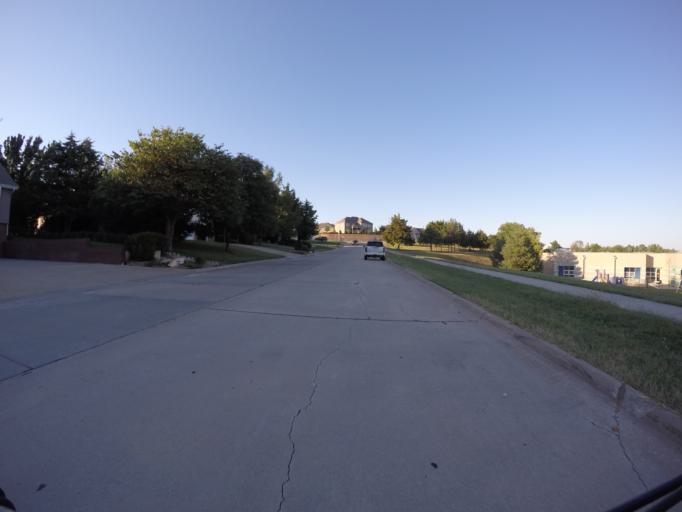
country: US
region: Kansas
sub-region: Riley County
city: Manhattan
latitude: 39.2123
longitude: -96.6254
